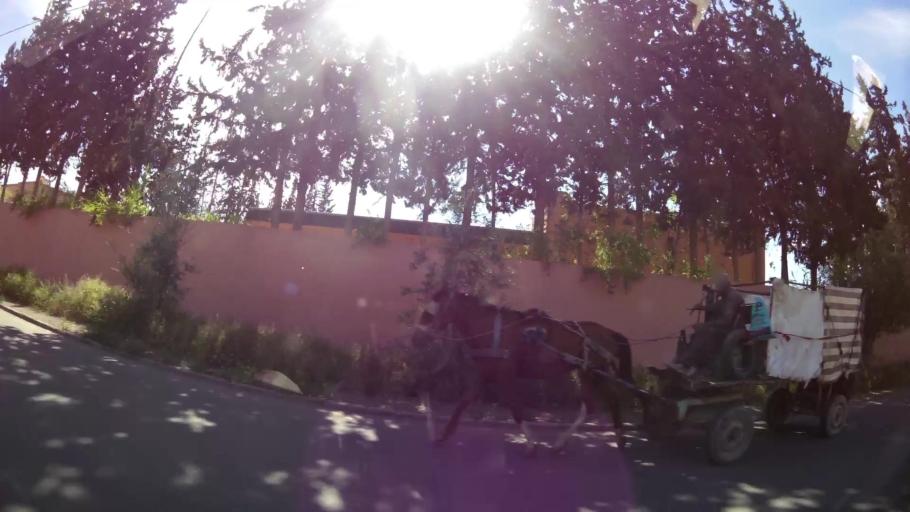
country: MA
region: Marrakech-Tensift-Al Haouz
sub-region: Marrakech
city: Marrakesh
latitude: 31.6455
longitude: -8.0473
